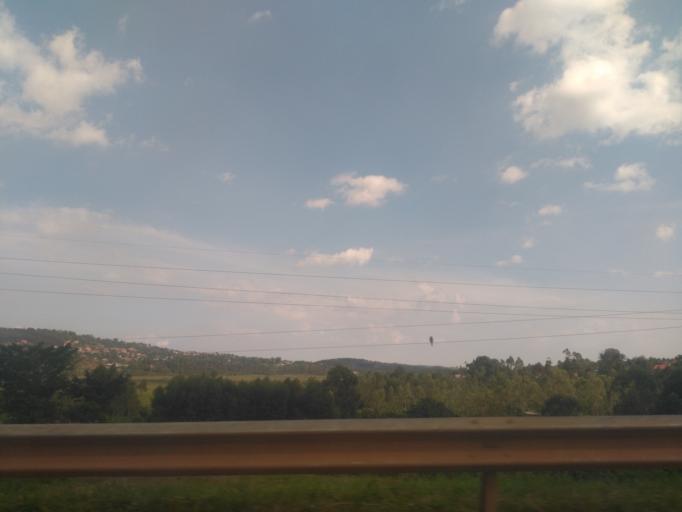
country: UG
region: Central Region
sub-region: Wakiso District
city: Kajansi
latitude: 0.2701
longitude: 32.4382
